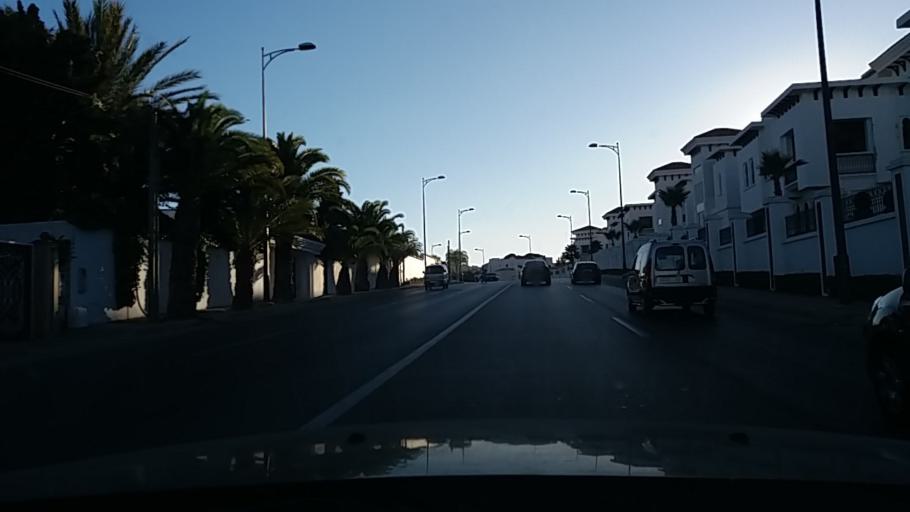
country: MA
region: Tanger-Tetouan
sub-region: Tanger-Assilah
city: Tangier
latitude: 35.7776
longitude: -5.8496
